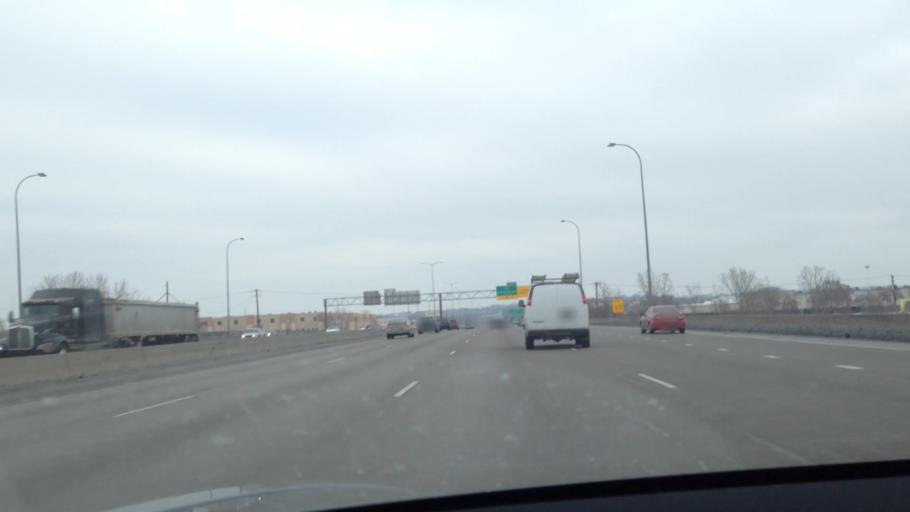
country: US
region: Minnesota
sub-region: Anoka County
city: Fridley
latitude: 45.0693
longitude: -93.2822
